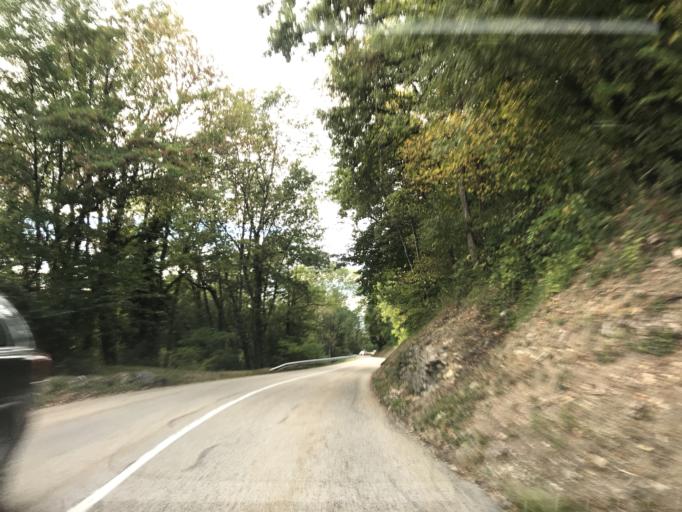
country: FR
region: Rhone-Alpes
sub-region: Departement de la Haute-Savoie
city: Menthon-Saint-Bernard
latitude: 45.8668
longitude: 6.1939
